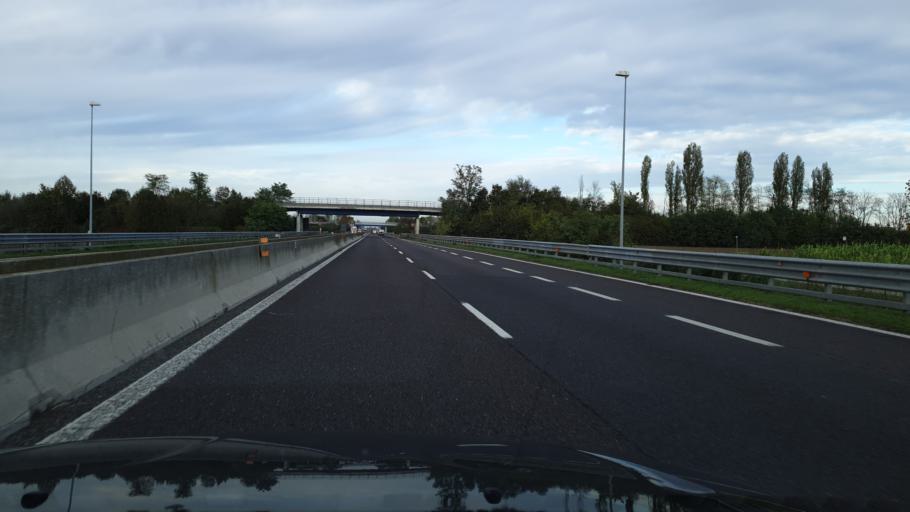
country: IT
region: Veneto
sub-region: Provincia di Rovigo
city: Costa di Rovigo
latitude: 45.0432
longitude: 11.7114
